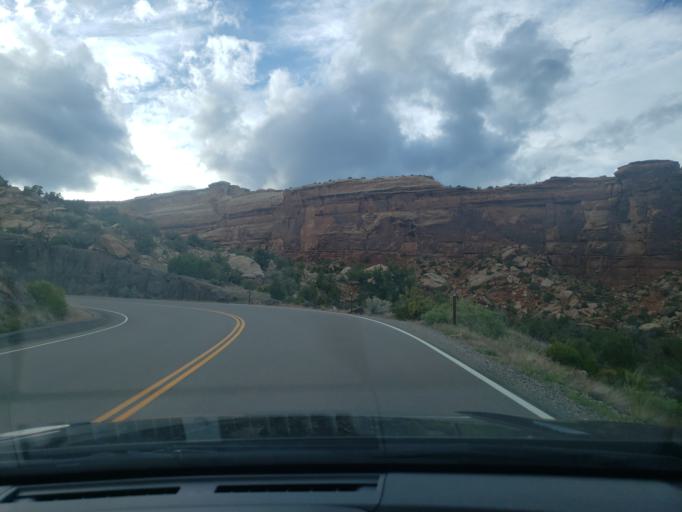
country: US
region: Colorado
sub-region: Mesa County
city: Redlands
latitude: 39.0282
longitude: -108.6390
